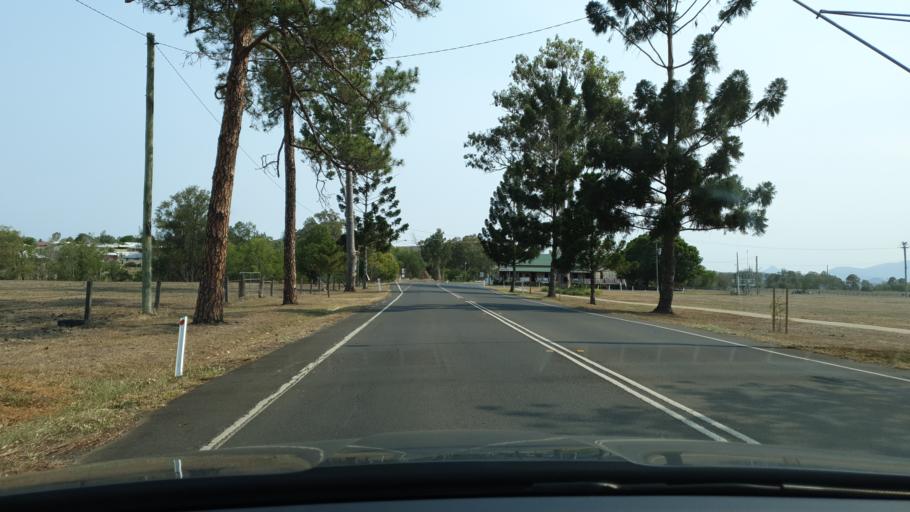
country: AU
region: Queensland
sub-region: Ipswich
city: Deebing Heights
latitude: -28.0029
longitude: 152.6813
